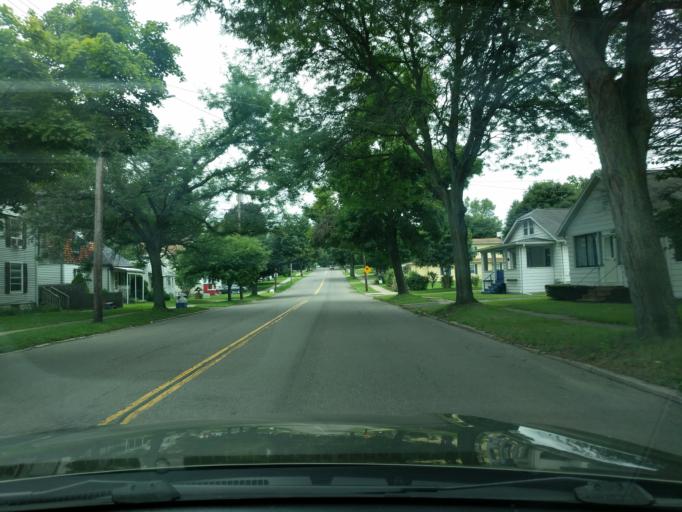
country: US
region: New York
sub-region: Chemung County
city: Elmira
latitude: 42.1053
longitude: -76.8185
